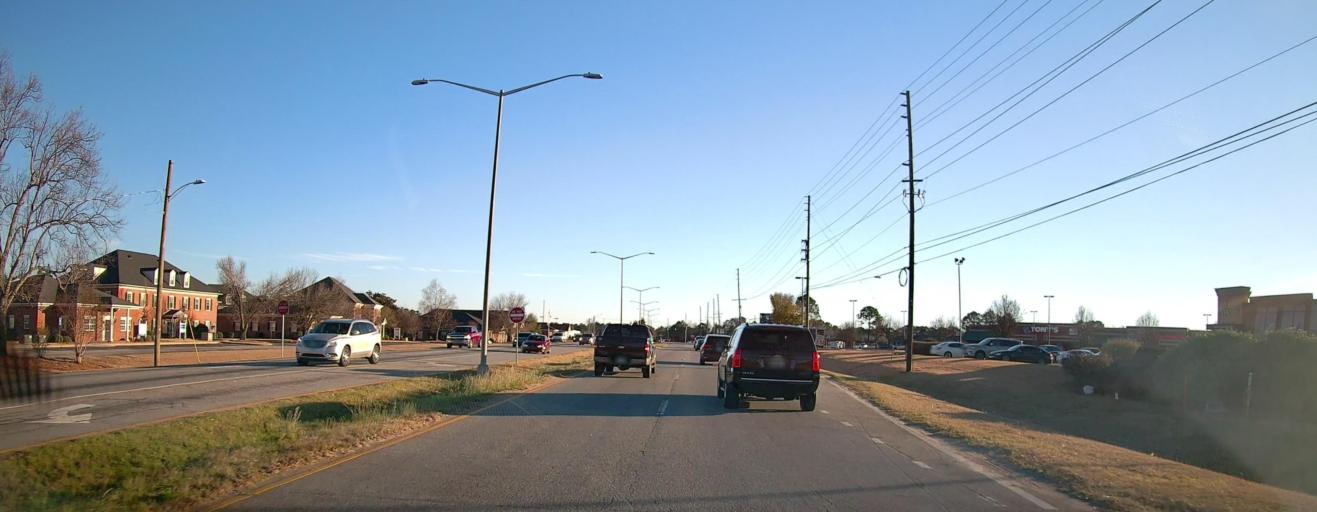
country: US
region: Georgia
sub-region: Dougherty County
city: Albany
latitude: 31.6134
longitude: -84.2231
